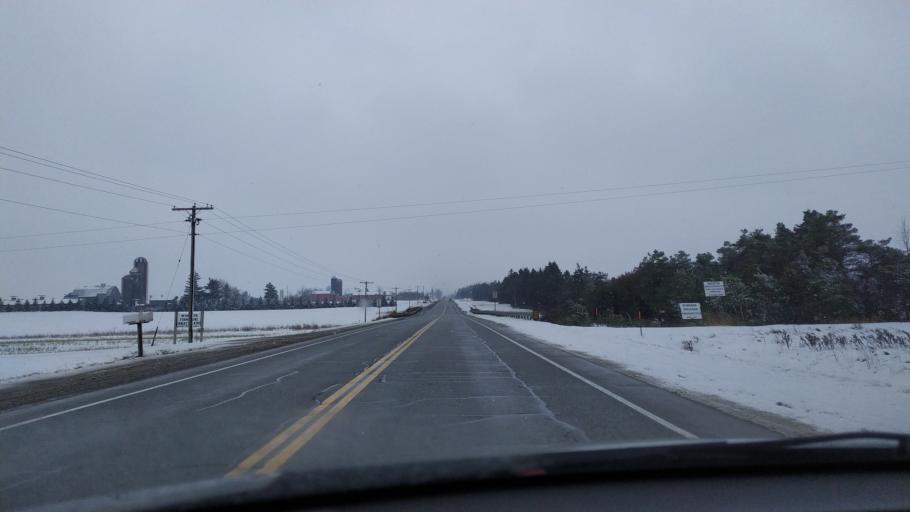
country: CA
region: Ontario
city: Waterloo
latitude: 43.6287
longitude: -80.7070
